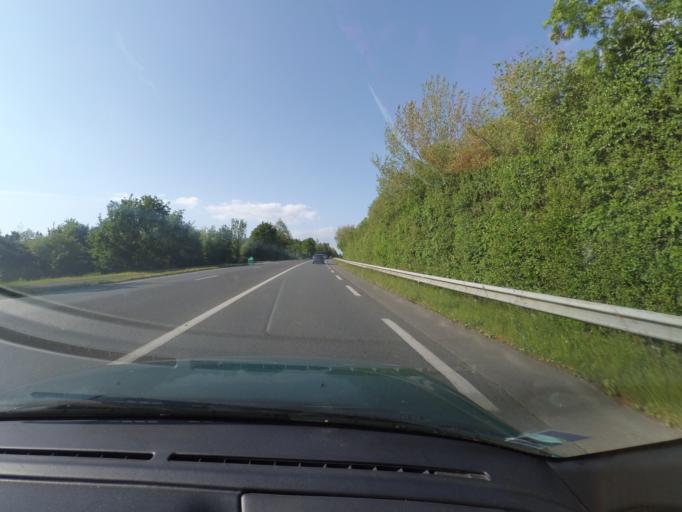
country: FR
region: Pays de la Loire
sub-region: Departement de la Vendee
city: Aubigny
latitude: 46.6067
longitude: -1.4453
